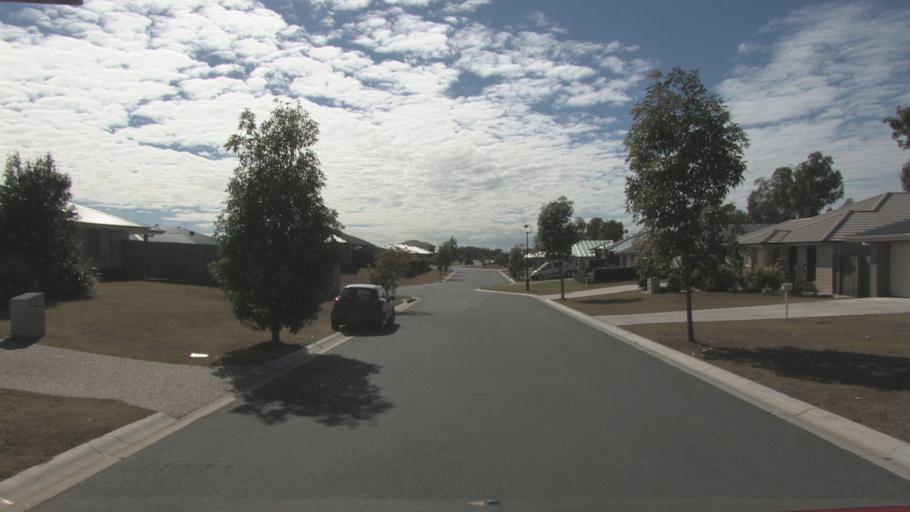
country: AU
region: Queensland
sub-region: Logan
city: Chambers Flat
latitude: -27.7757
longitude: 153.1022
